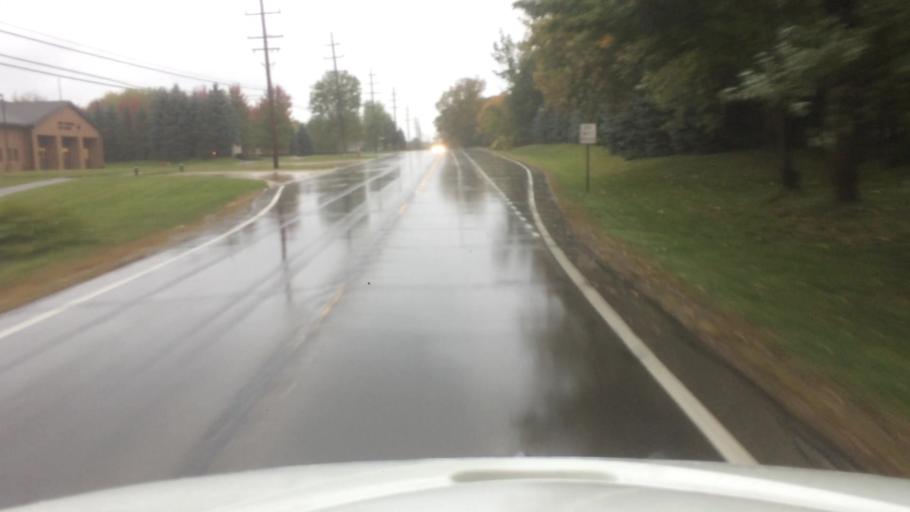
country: US
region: Michigan
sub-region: Oakland County
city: Oxford
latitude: 42.7763
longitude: -83.3195
